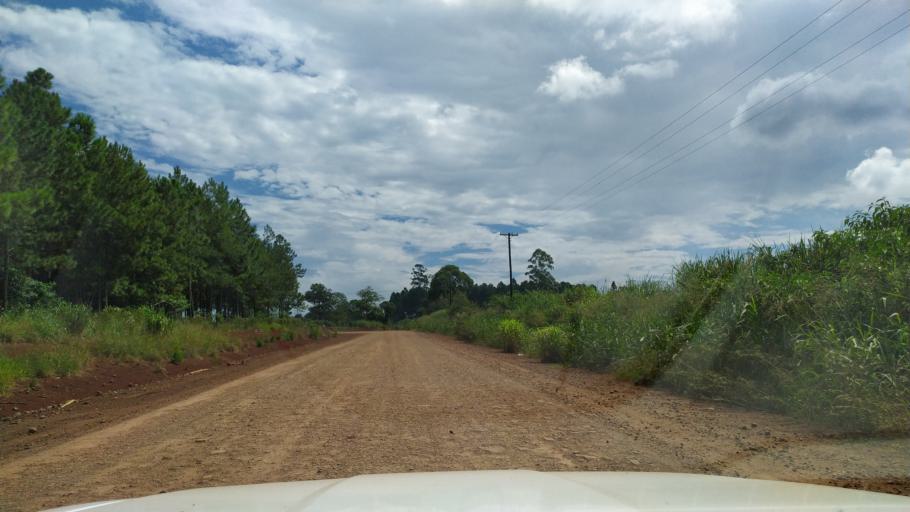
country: AR
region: Misiones
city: Puerto Piray
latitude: -26.5341
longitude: -54.6670
